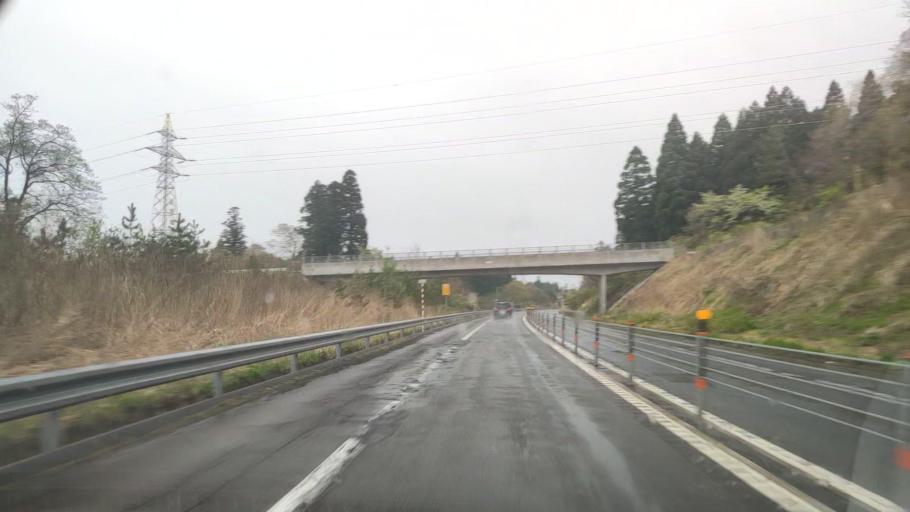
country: JP
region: Akita
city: Noshiromachi
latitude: 40.1679
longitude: 140.0506
